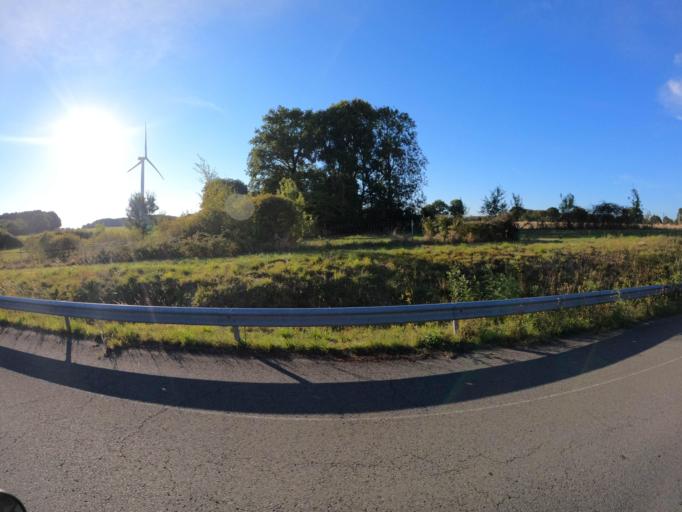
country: FR
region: Pays de la Loire
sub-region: Departement de Maine-et-Loire
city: Chemille-Melay
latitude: 47.1896
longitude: -0.7766
